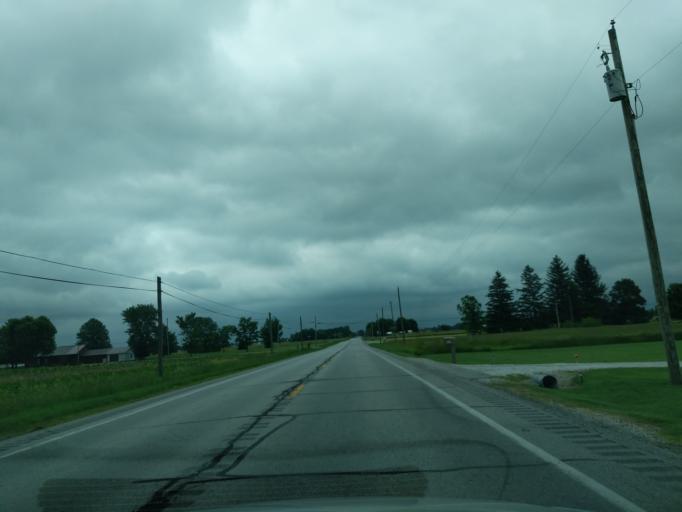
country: US
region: Indiana
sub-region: Madison County
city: Frankton
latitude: 40.2775
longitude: -85.7584
